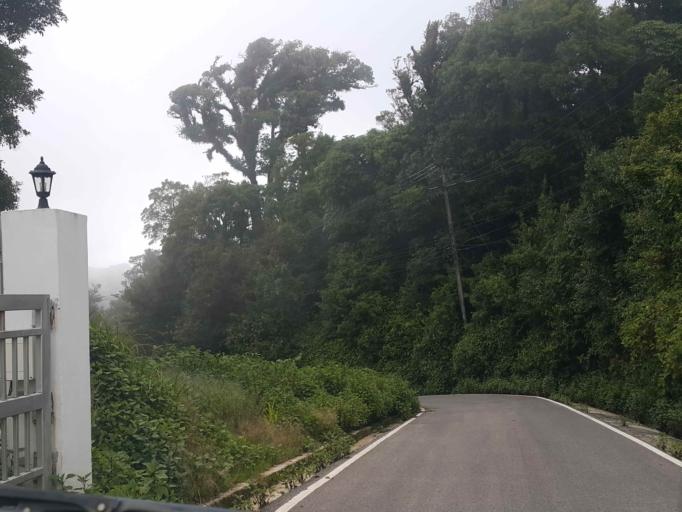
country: TH
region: Chiang Mai
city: Mae Chaem
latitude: 18.5739
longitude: 98.4823
